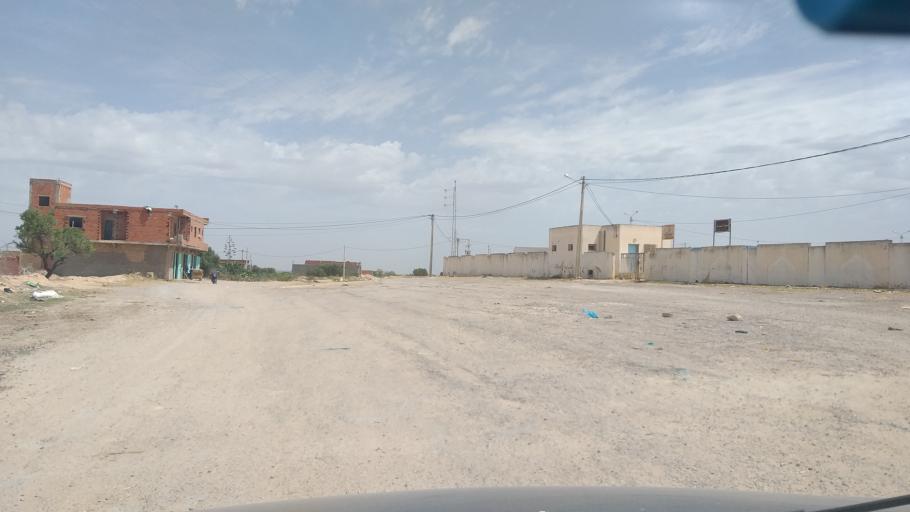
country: TN
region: Al Mahdiyah
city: El Jem
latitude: 35.3113
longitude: 10.7038
